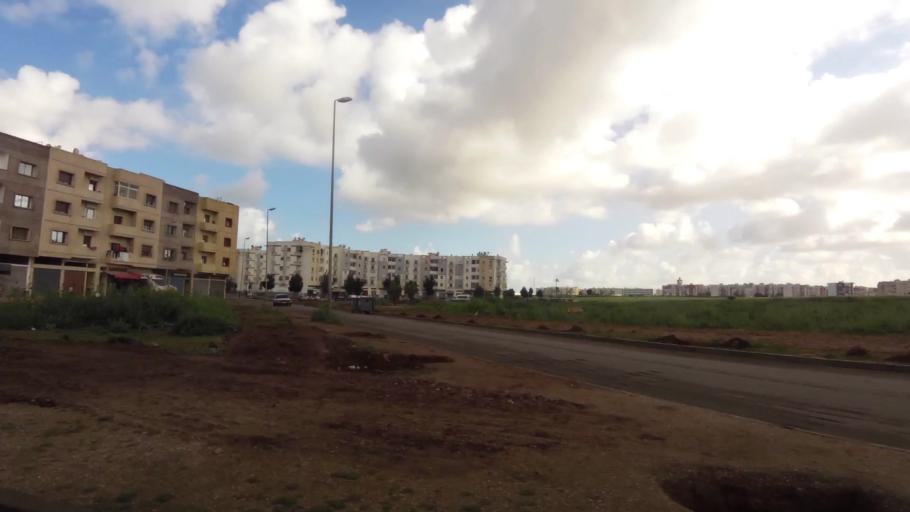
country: MA
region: Grand Casablanca
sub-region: Nouaceur
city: Bouskoura
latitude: 33.5345
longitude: -7.7022
